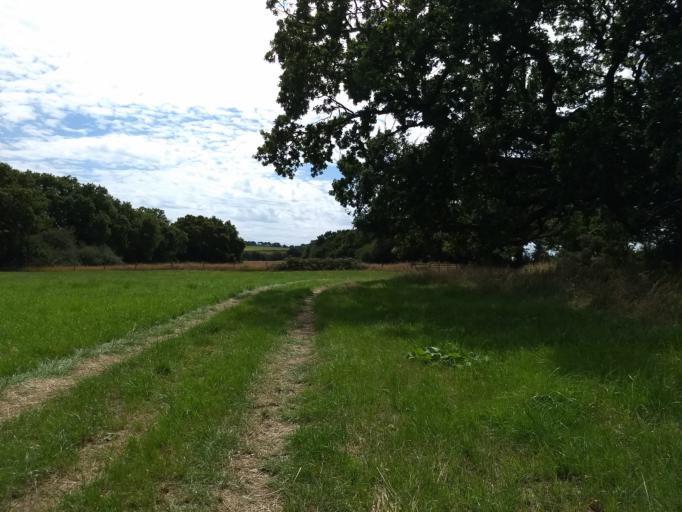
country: GB
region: England
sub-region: Isle of Wight
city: Newport
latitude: 50.7146
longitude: -1.2683
